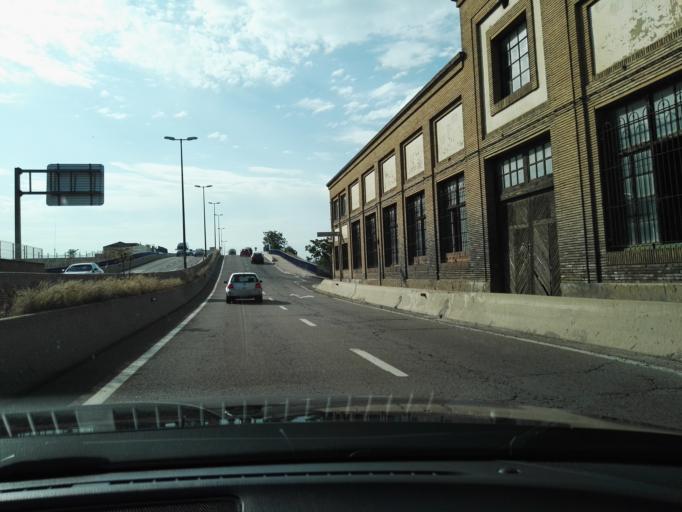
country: ES
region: Aragon
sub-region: Provincia de Zaragoza
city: Zaragoza
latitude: 41.6296
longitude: -0.8552
